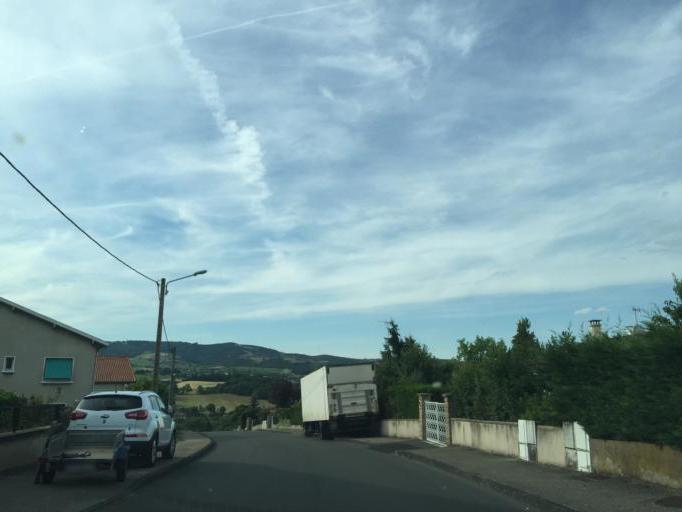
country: FR
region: Rhone-Alpes
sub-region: Departement de la Loire
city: Saint-Chamond
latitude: 45.4789
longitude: 4.5302
